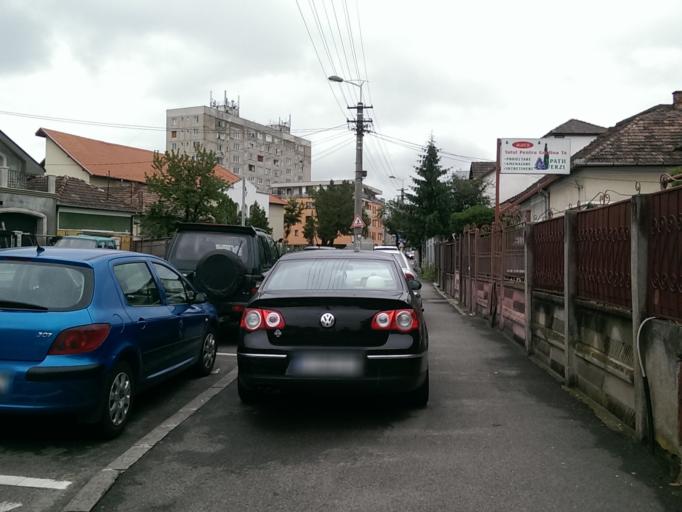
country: RO
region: Cluj
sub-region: Municipiul Cluj-Napoca
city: Cluj-Napoca
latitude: 46.7647
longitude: 23.6116
